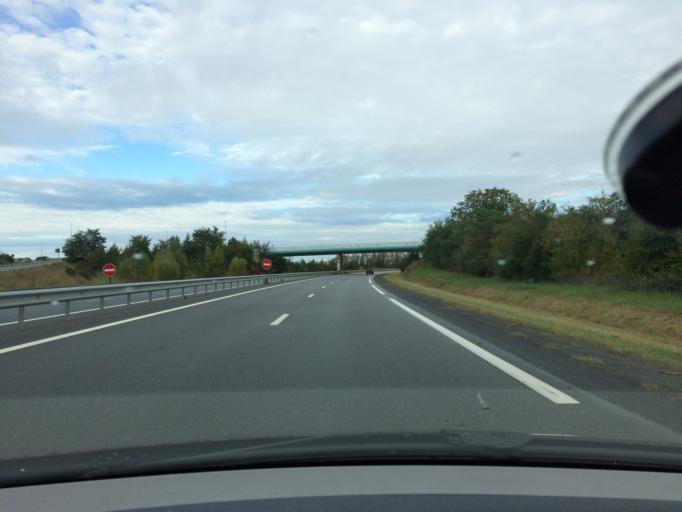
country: FR
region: Brittany
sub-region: Departement d'Ille-et-Vilaine
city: Corps-Nuds
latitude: 47.9781
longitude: -1.5590
